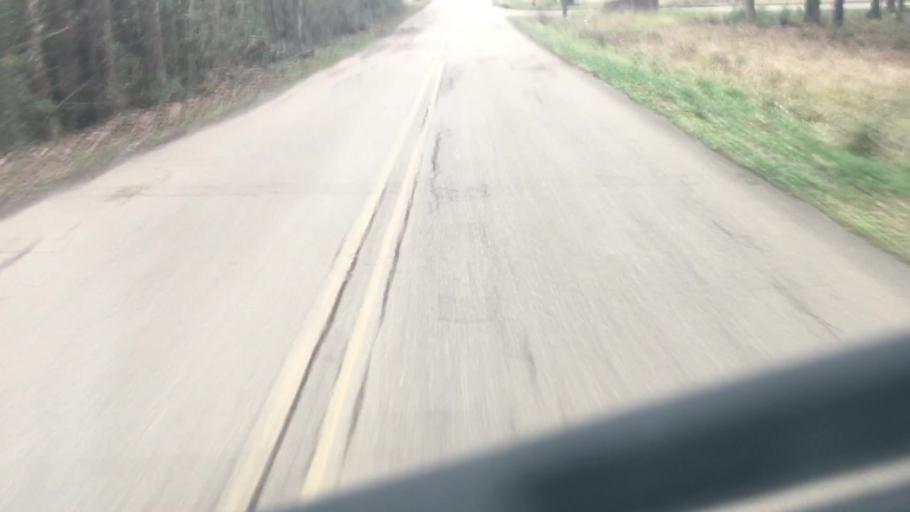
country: US
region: Alabama
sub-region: Walker County
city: Jasper
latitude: 33.8320
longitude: -87.2253
